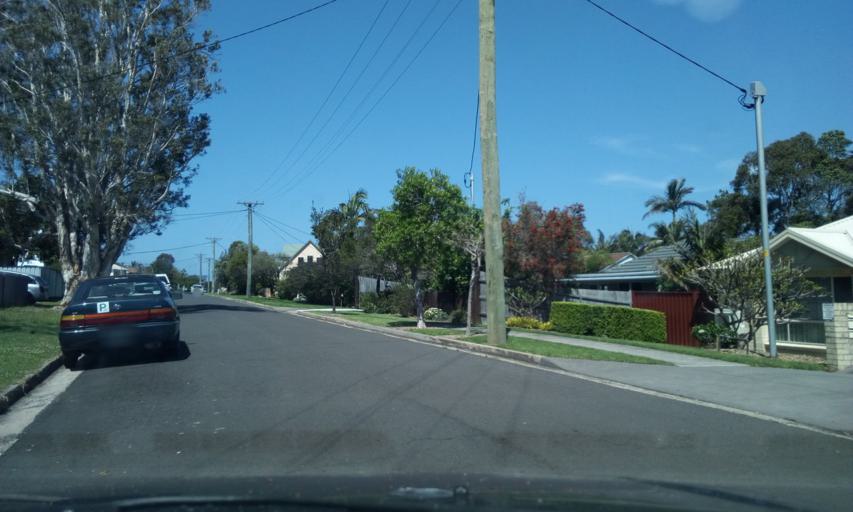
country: AU
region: New South Wales
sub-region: Wollongong
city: Bulli
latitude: -34.3311
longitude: 150.9190
